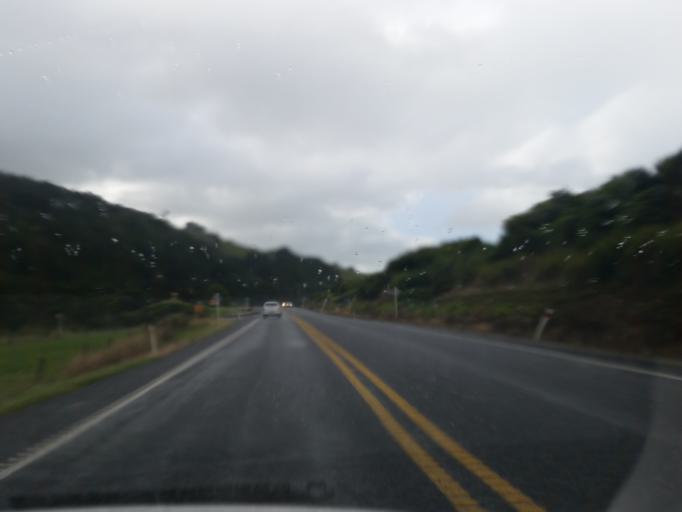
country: NZ
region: Waikato
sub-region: Hauraki District
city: Ngatea
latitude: -37.2831
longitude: 175.3232
